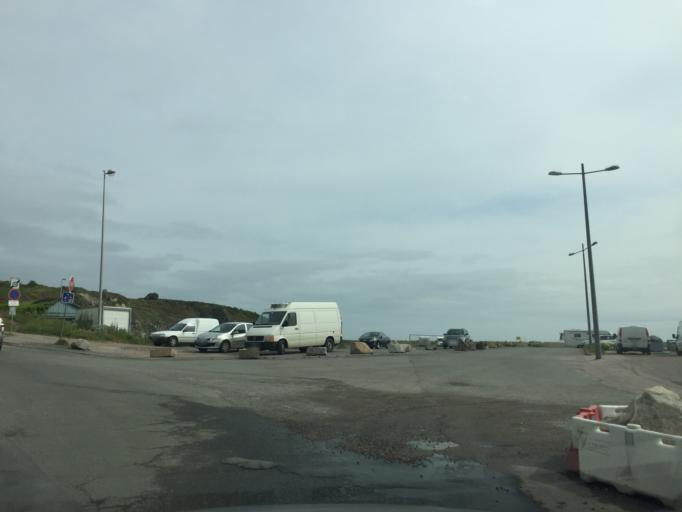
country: FR
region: Brittany
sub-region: Departement des Cotes-d'Armor
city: Saint-Cast-le-Guildo
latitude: 48.6416
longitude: -2.2454
